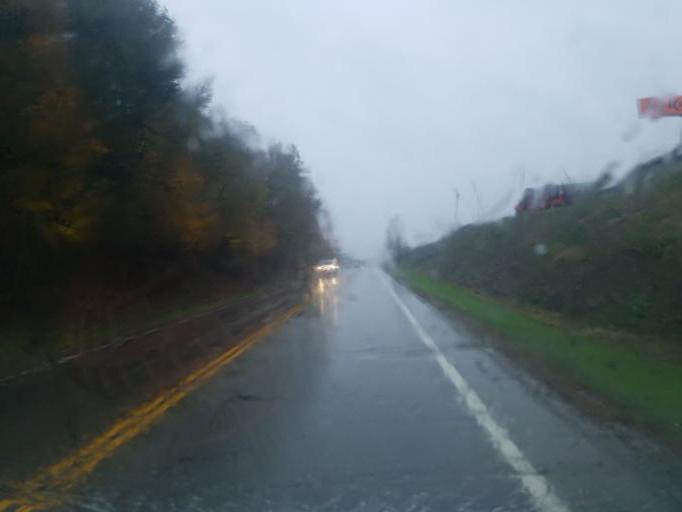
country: US
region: Ohio
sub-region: Muskingum County
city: North Zanesville
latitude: 39.9816
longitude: -82.0529
